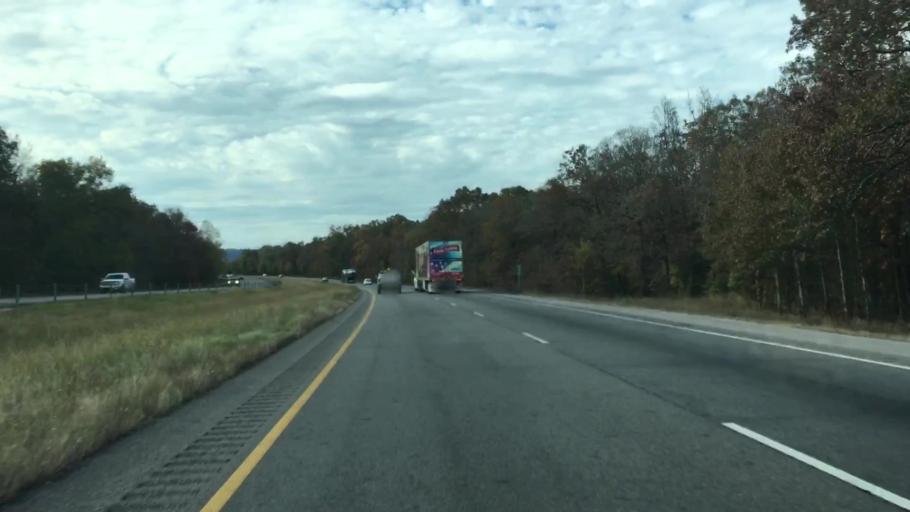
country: US
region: Arkansas
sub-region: Pope County
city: Atkins
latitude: 35.2449
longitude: -92.8644
